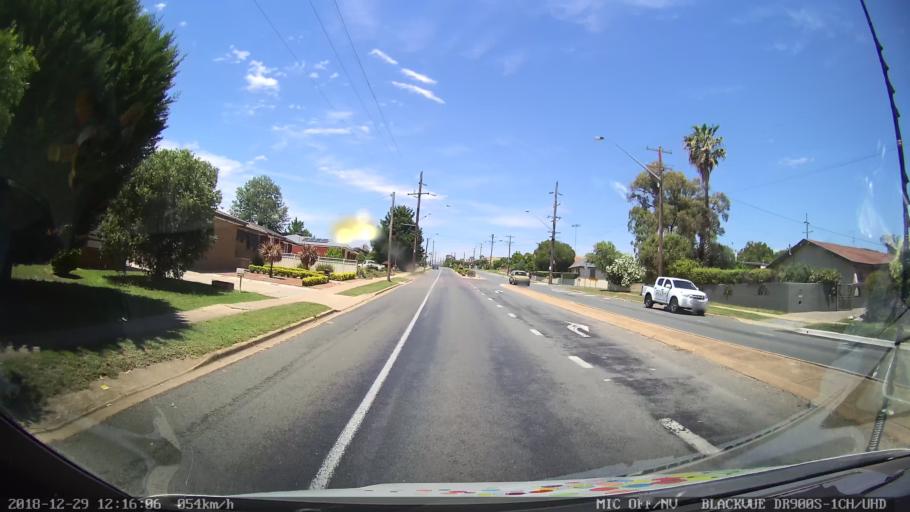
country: AU
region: New South Wales
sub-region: Queanbeyan
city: Queanbeyan
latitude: -35.3669
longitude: 149.2334
